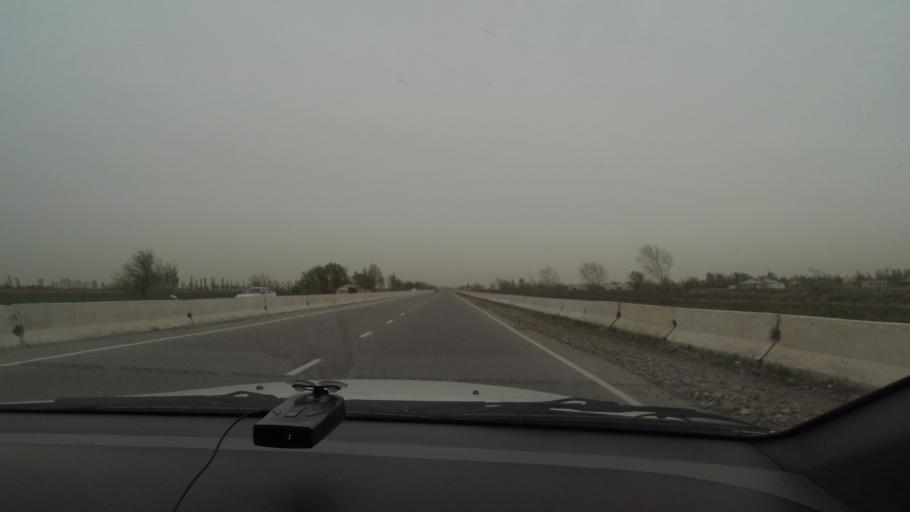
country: UZ
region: Jizzax
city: Gagarin
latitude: 40.4875
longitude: 68.2933
